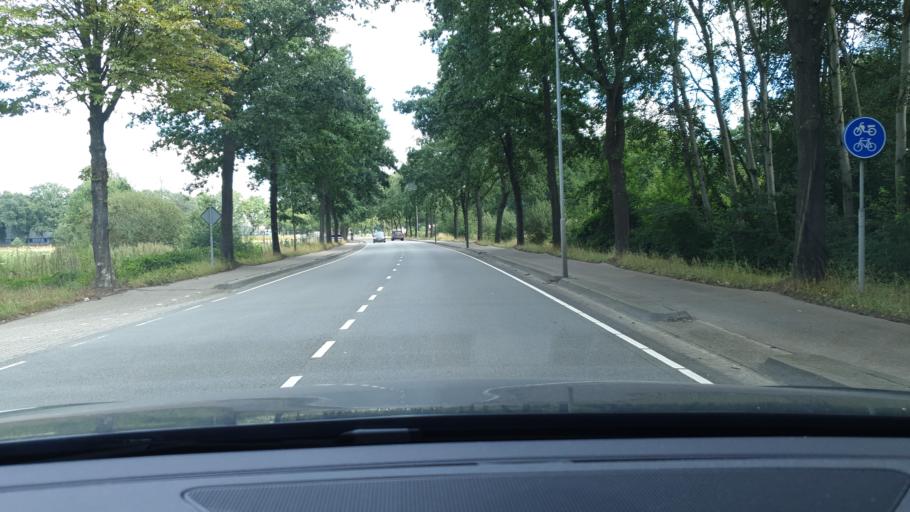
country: NL
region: North Brabant
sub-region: Gemeente Valkenswaard
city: Valkenswaard
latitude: 51.3428
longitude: 5.4797
